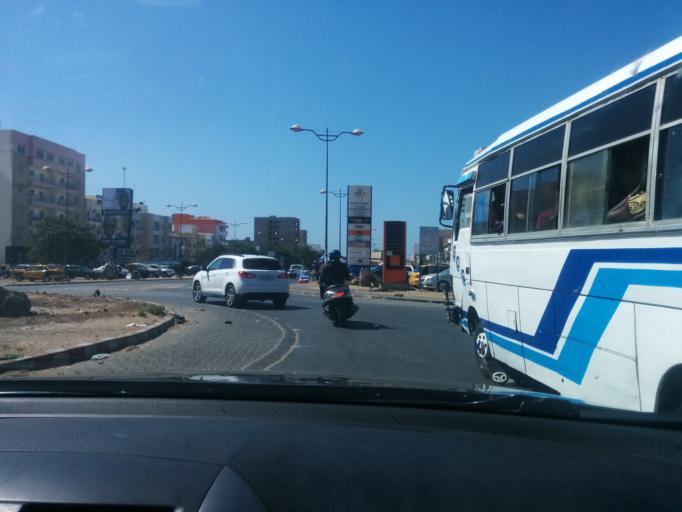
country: SN
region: Dakar
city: Grand Dakar
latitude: 14.7182
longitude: -17.4664
